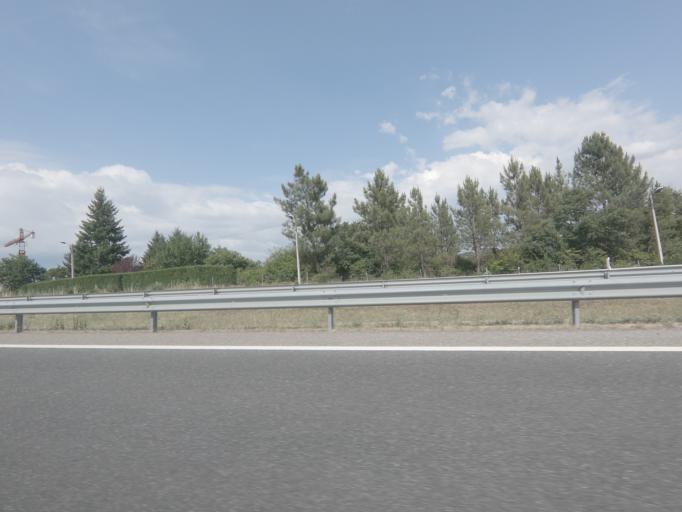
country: ES
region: Galicia
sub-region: Provincia de Ourense
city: Ourense
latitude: 42.3194
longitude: -7.8867
